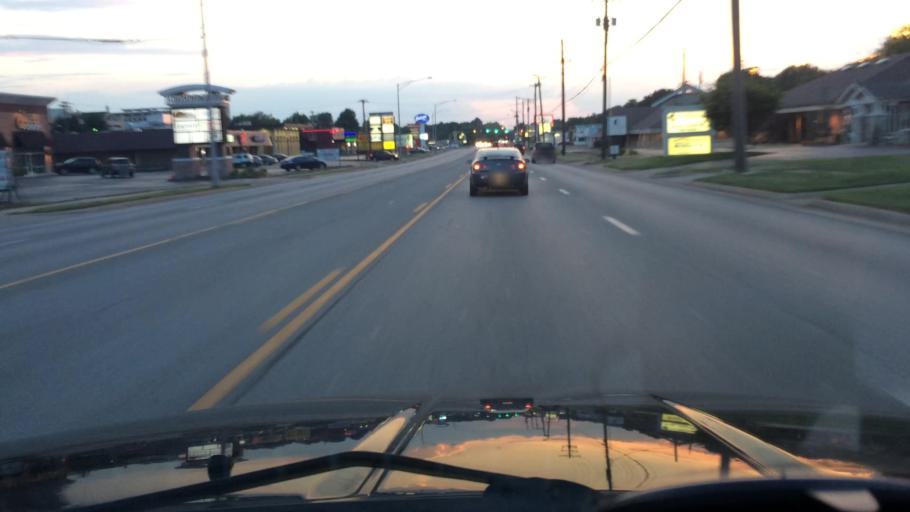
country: US
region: Missouri
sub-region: Greene County
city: Springfield
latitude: 37.1818
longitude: -93.2681
